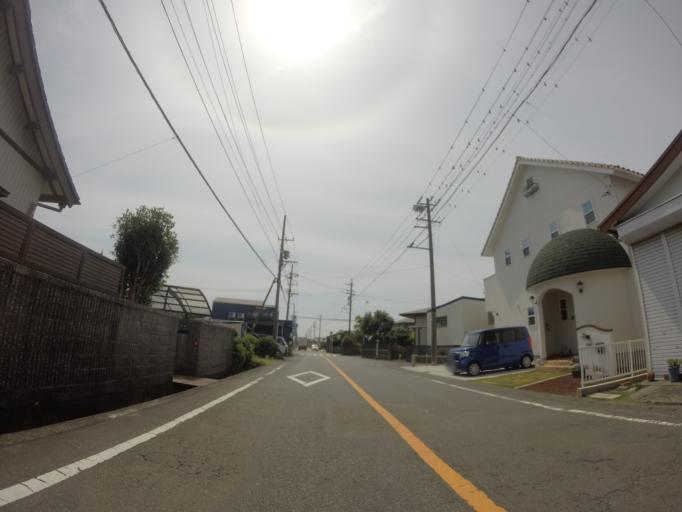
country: JP
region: Shizuoka
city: Fujieda
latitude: 34.8113
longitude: 138.2835
